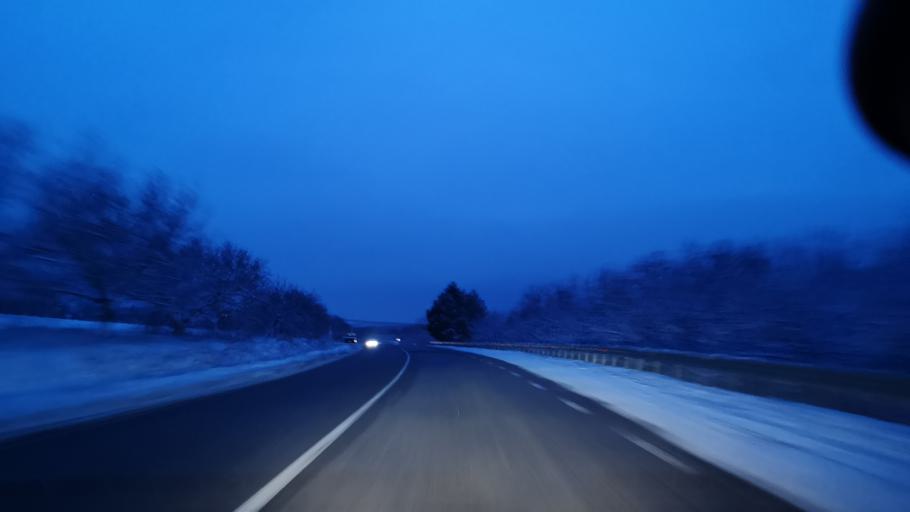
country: MD
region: Orhei
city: Orhei
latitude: 47.5535
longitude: 28.7947
